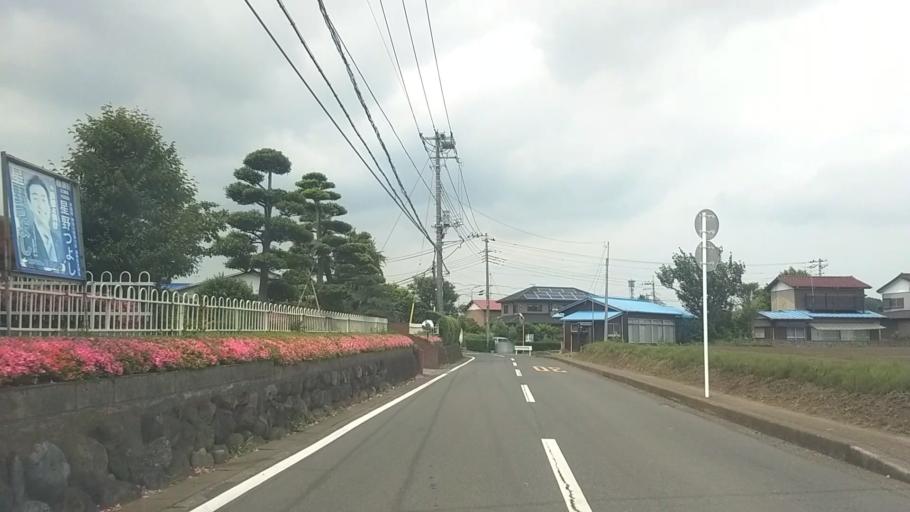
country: JP
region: Kanagawa
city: Chigasaki
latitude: 35.3882
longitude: 139.4140
